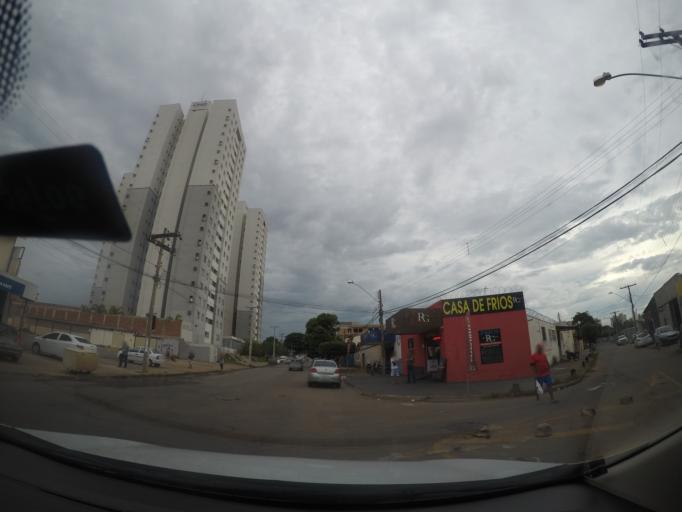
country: BR
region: Goias
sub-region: Goiania
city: Goiania
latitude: -16.6572
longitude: -49.2448
